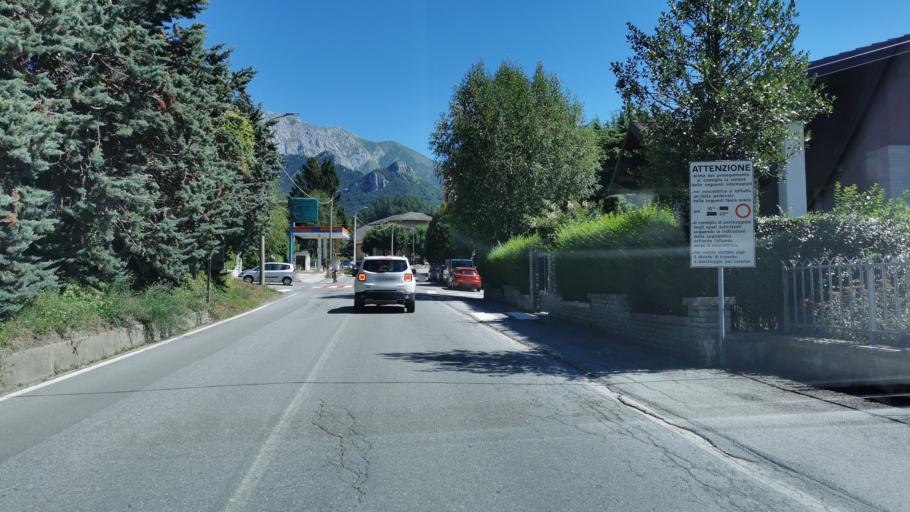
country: IT
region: Piedmont
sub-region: Provincia di Cuneo
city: Entracque
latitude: 44.2440
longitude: 7.3968
